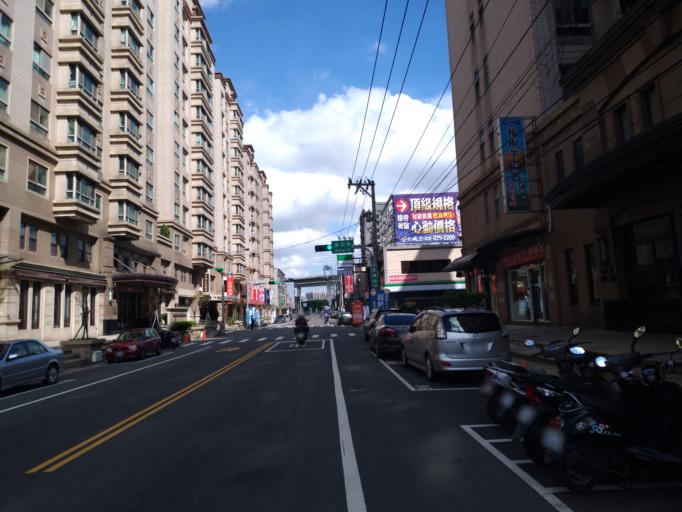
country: TW
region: Taiwan
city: Daxi
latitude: 24.9130
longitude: 121.1617
